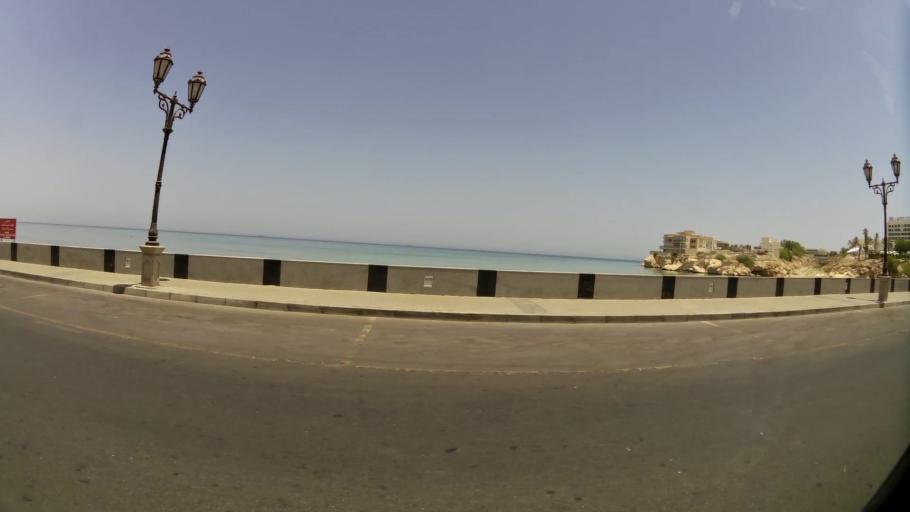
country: OM
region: Muhafazat Masqat
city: Bawshar
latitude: 23.6260
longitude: 58.4812
